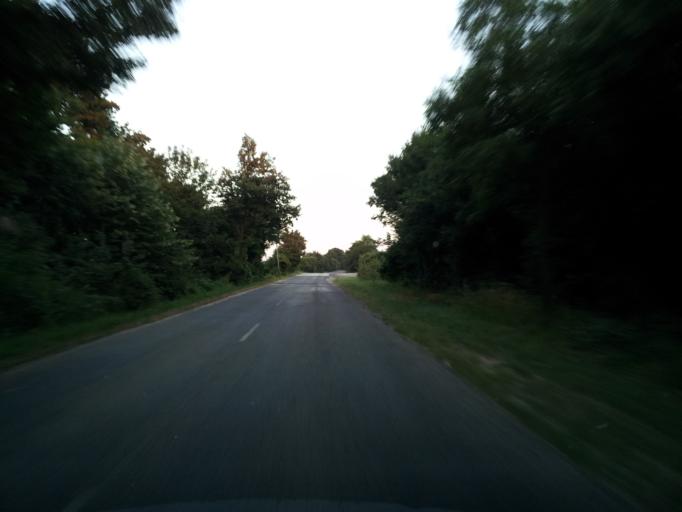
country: HU
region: Fejer
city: Szarliget
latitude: 47.5308
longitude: 18.4611
